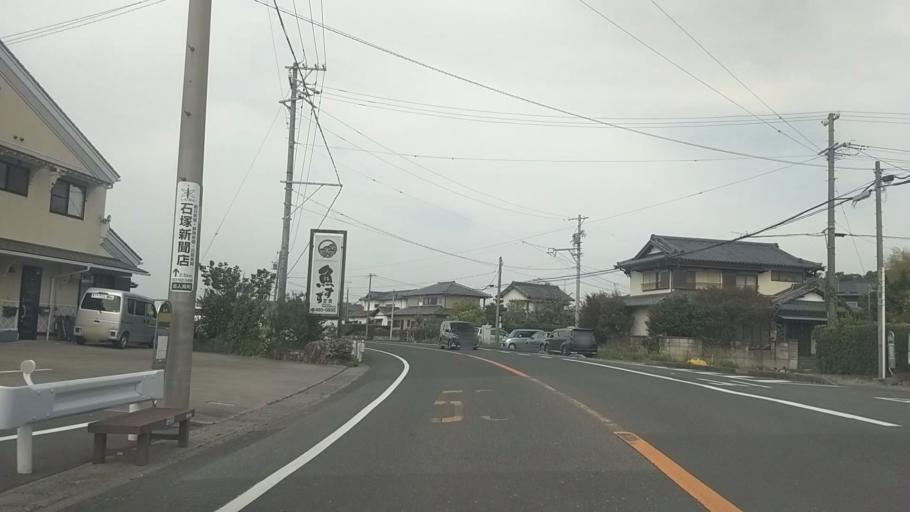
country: JP
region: Shizuoka
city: Hamamatsu
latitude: 34.7305
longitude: 137.6355
